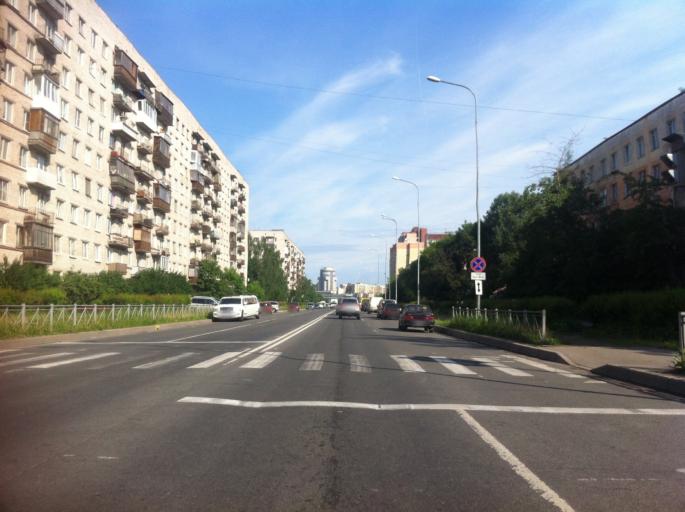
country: RU
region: St.-Petersburg
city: Dachnoye
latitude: 59.8444
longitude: 30.2326
